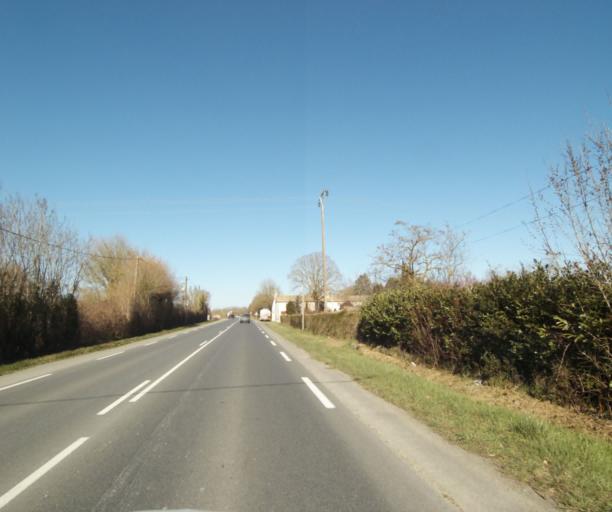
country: FR
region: Poitou-Charentes
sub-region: Departement des Deux-Sevres
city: Niort
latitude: 46.2915
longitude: -0.4659
